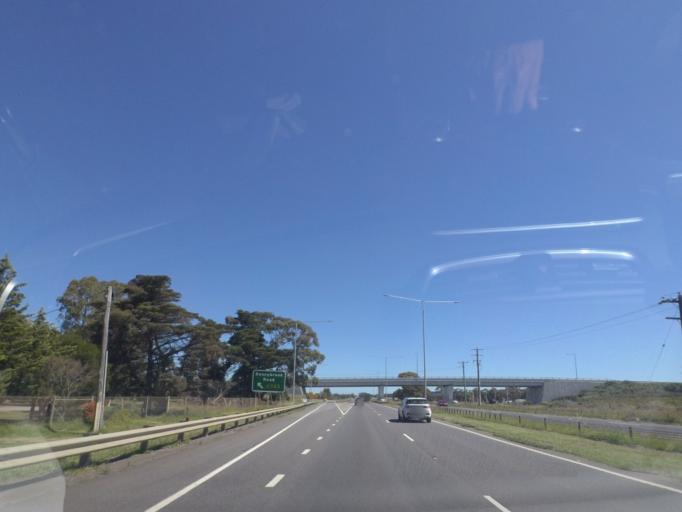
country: AU
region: Victoria
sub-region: Hume
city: Craigieburn
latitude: -37.5390
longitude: 144.9458
